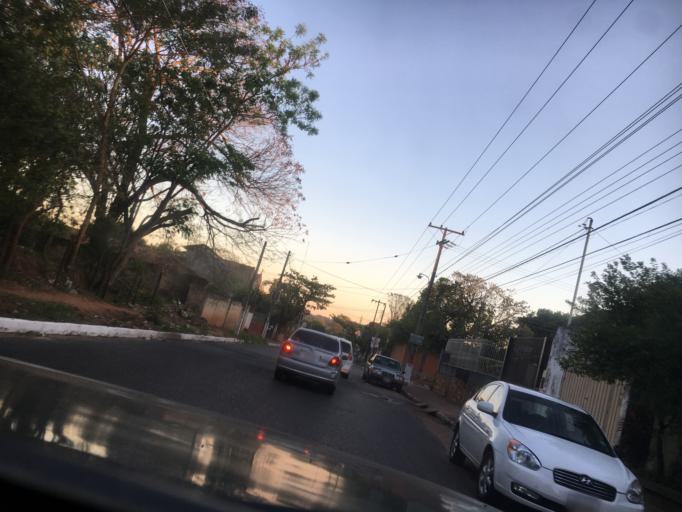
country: PY
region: Central
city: Lambare
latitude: -25.3433
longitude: -57.6027
